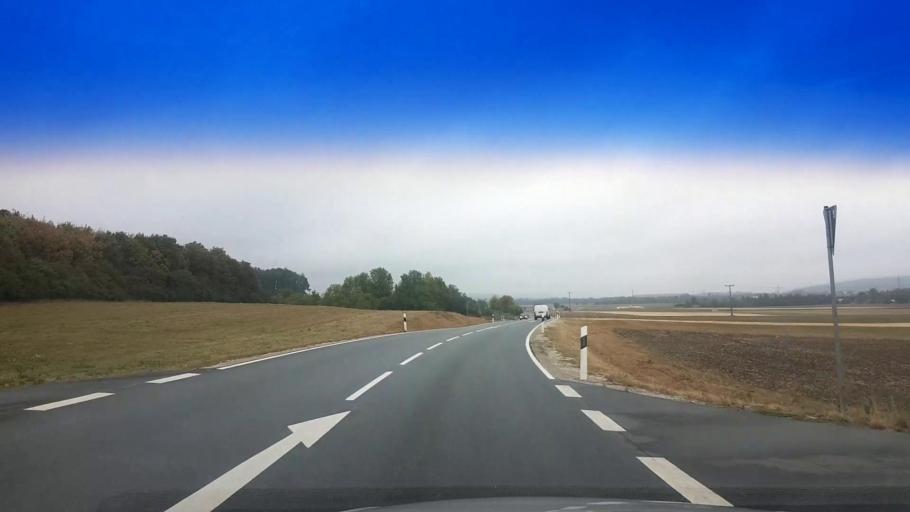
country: DE
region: Bavaria
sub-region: Upper Franconia
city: Buttenheim
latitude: 49.7930
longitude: 11.0375
